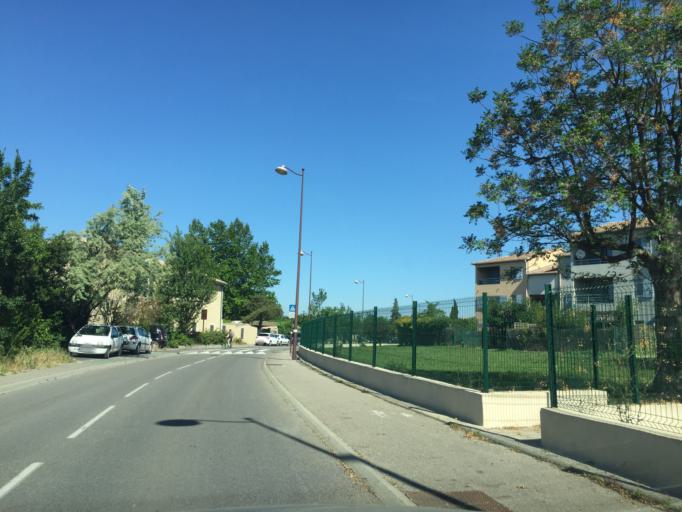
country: FR
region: Provence-Alpes-Cote d'Azur
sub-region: Departement du Vaucluse
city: L'Isle-sur-la-Sorgue
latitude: 43.9227
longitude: 5.0402
